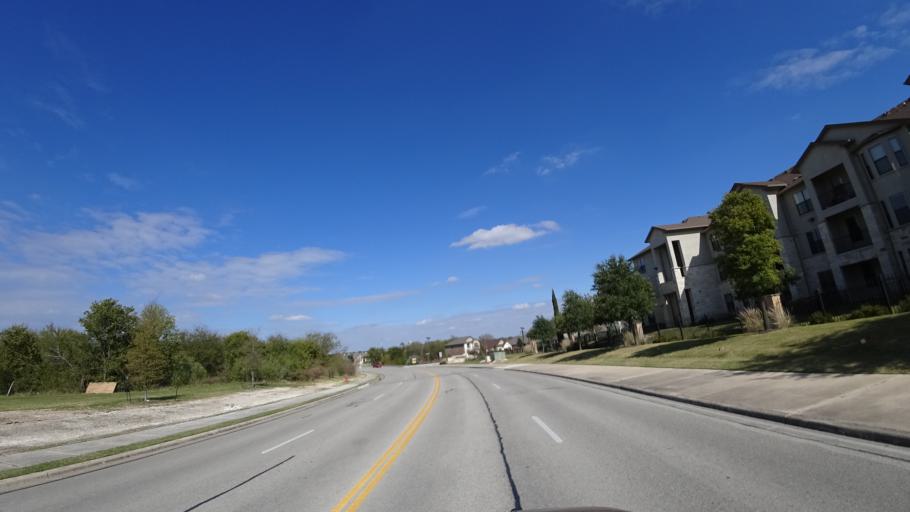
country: US
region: Texas
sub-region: Travis County
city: Pflugerville
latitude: 30.4493
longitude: -97.6300
